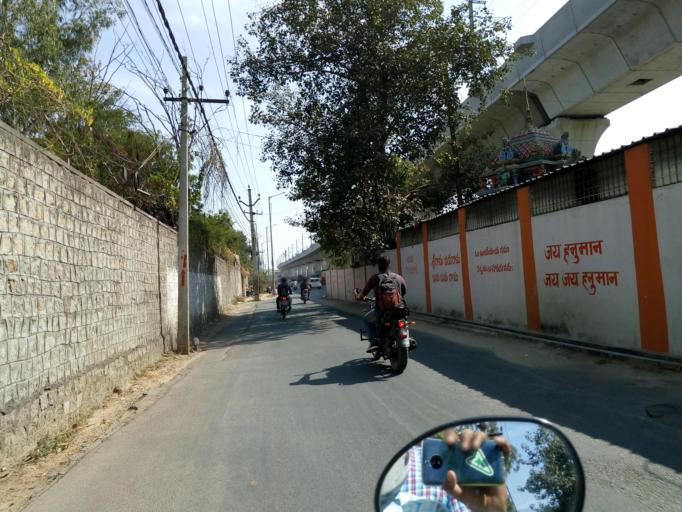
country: IN
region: Telangana
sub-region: Rangareddi
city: Uppal Kalan
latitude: 17.4120
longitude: 78.5498
